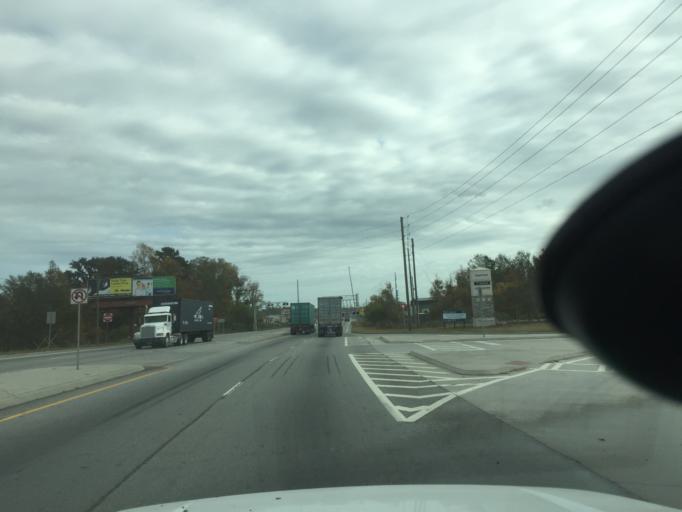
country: US
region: Georgia
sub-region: Chatham County
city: Garden City
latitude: 32.1262
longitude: -81.1794
